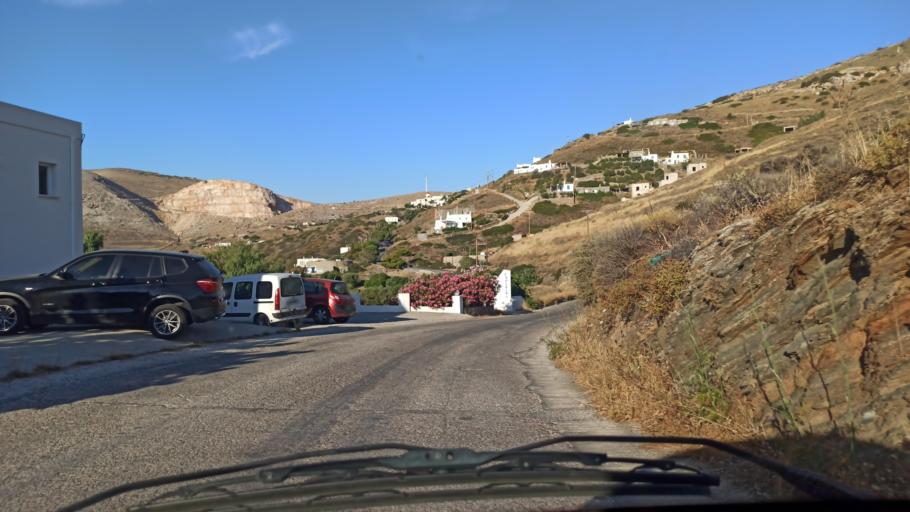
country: GR
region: South Aegean
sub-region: Nomos Kykladon
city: Ano Syros
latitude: 37.4420
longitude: 24.9032
